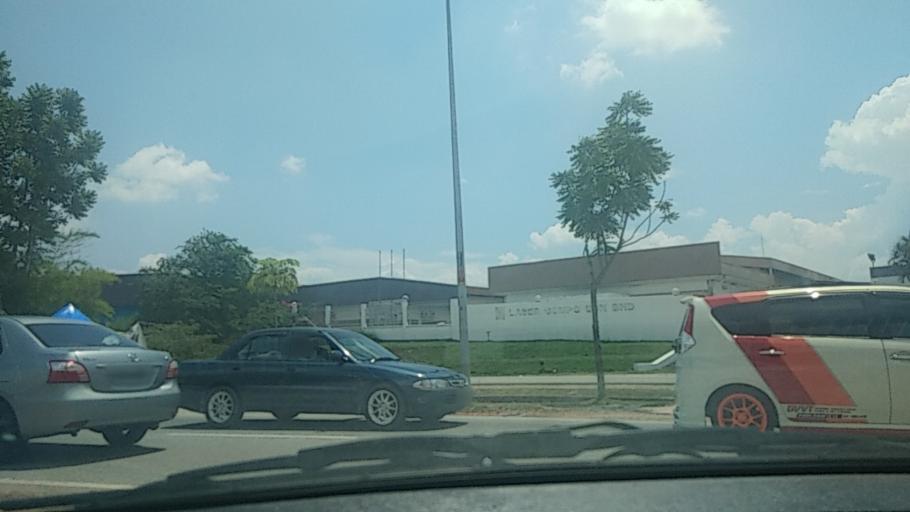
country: MY
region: Kedah
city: Sungai Petani
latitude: 5.6468
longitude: 100.5372
